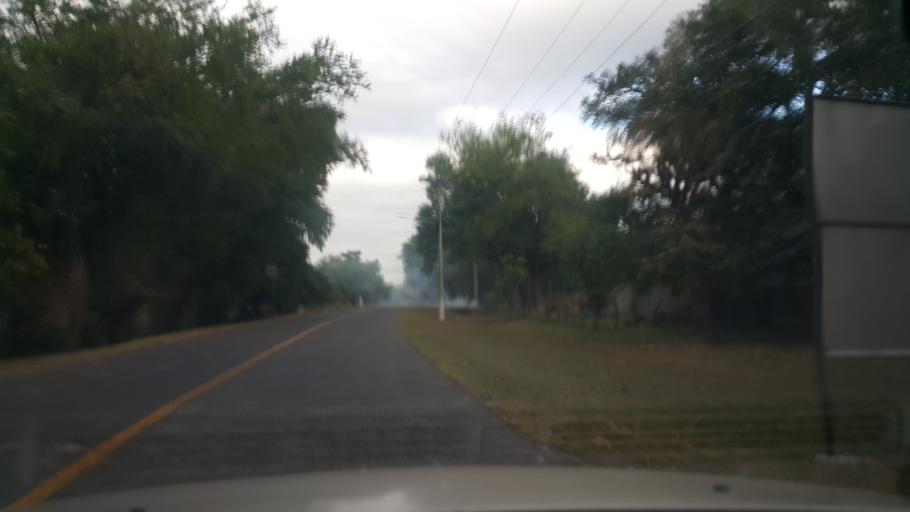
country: NI
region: Rivas
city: Moyogalpa
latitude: 11.5249
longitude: -85.7026
